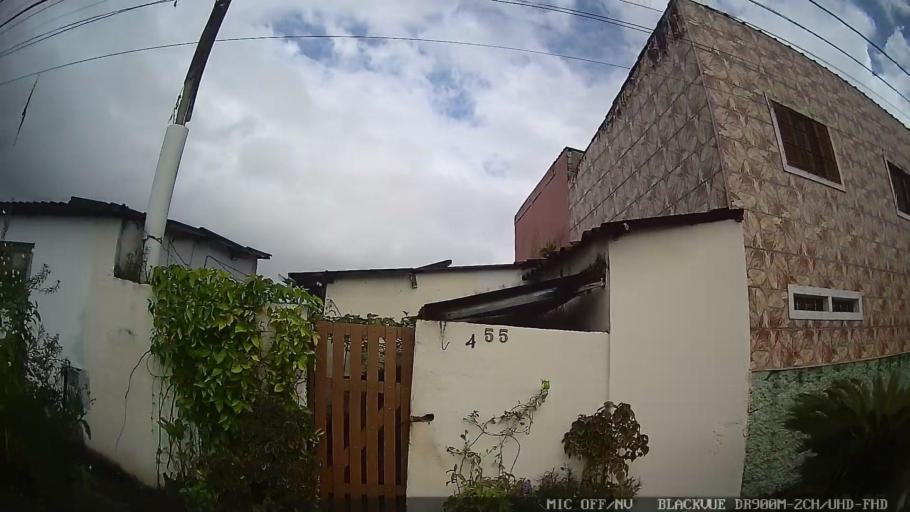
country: BR
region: Sao Paulo
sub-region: Itanhaem
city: Itanhaem
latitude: -24.1885
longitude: -46.8097
